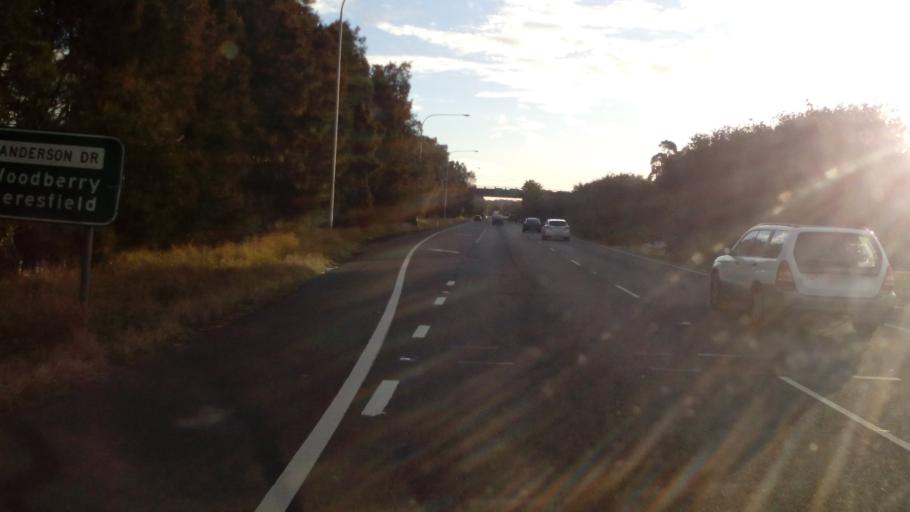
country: AU
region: New South Wales
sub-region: Newcastle
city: Beresfield
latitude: -32.8114
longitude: 151.6681
